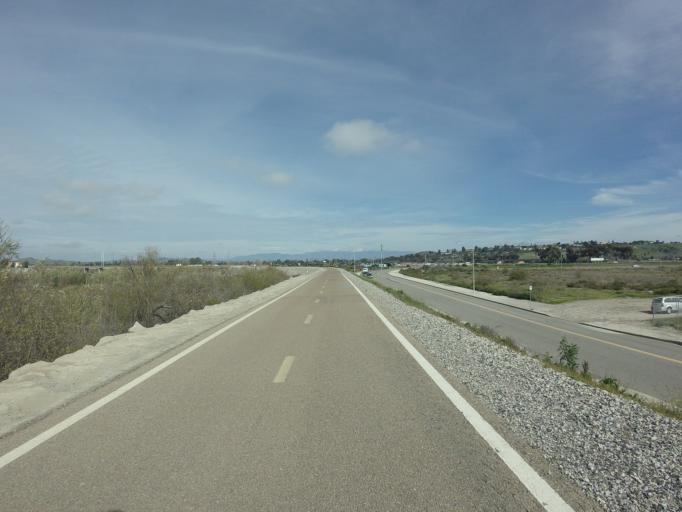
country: US
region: California
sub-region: San Diego County
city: Camp Pendleton South
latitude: 33.2208
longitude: -117.3474
